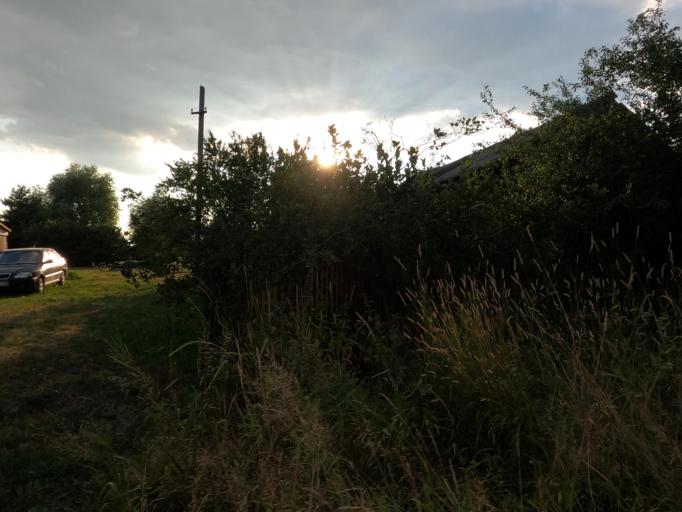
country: RU
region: Moskovskaya
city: Ashitkovo
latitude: 55.4173
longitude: 38.5797
